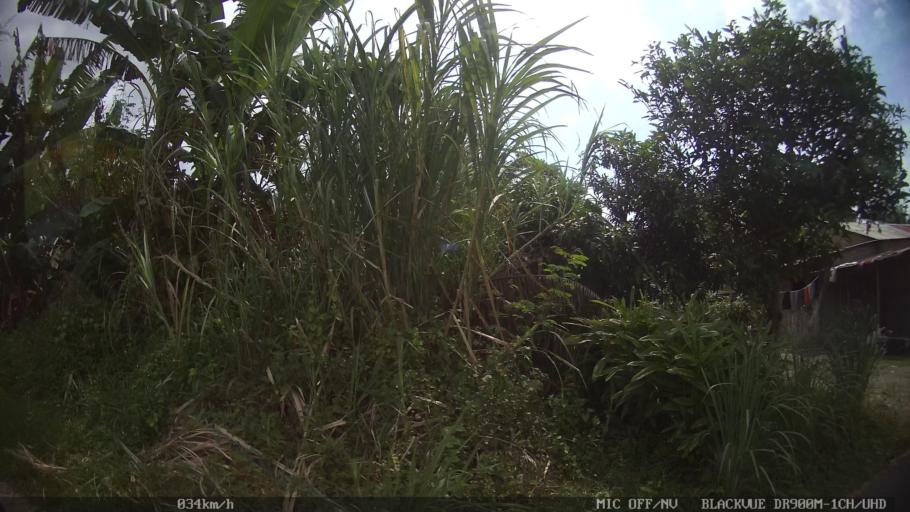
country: ID
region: North Sumatra
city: Percut
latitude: 3.5669
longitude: 98.8536
